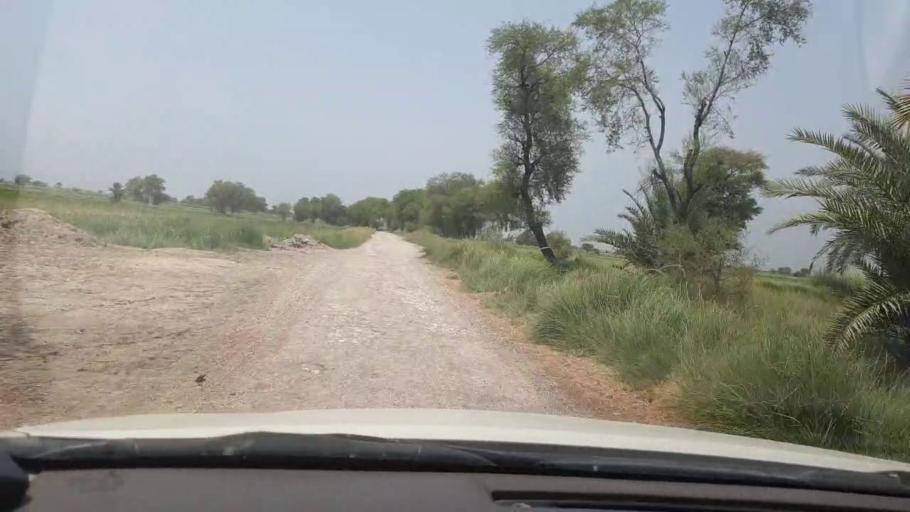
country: PK
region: Sindh
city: Garhi Yasin
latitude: 27.9109
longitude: 68.5561
